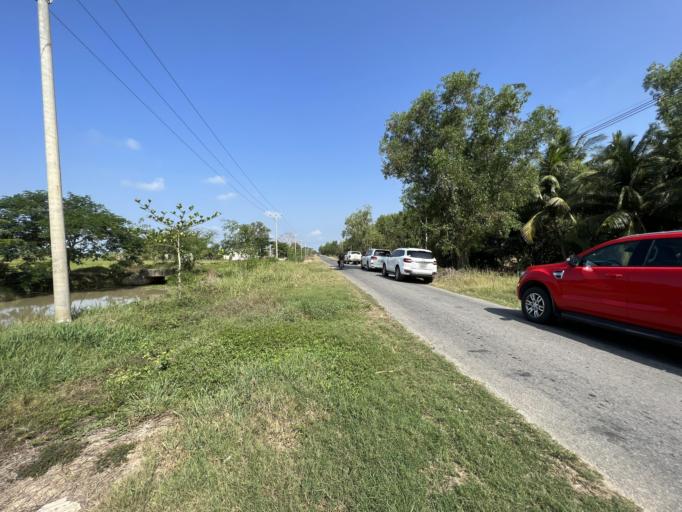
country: MM
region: Ayeyarwady
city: Kyaiklat
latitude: 16.4002
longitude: 95.8497
